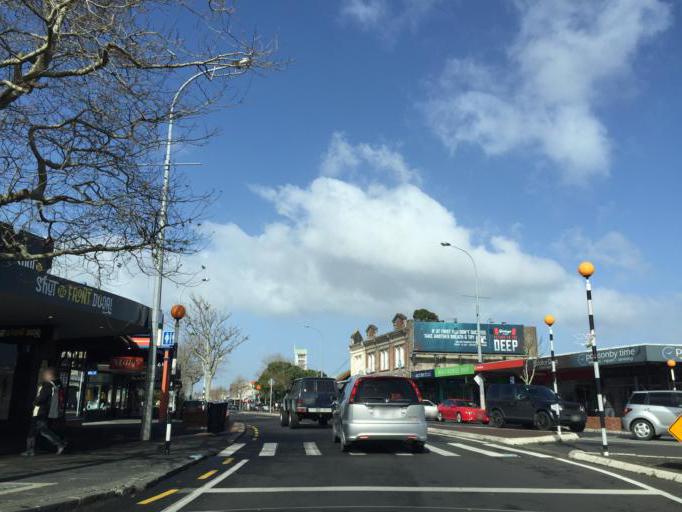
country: NZ
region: Auckland
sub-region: Auckland
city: Auckland
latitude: -36.8484
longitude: 174.7439
